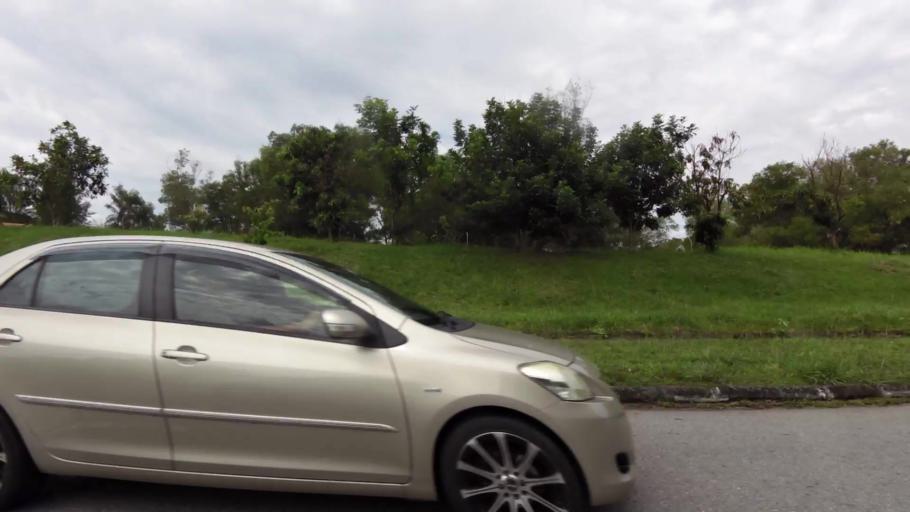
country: BN
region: Brunei and Muara
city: Bandar Seri Begawan
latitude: 4.8993
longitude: 114.9081
